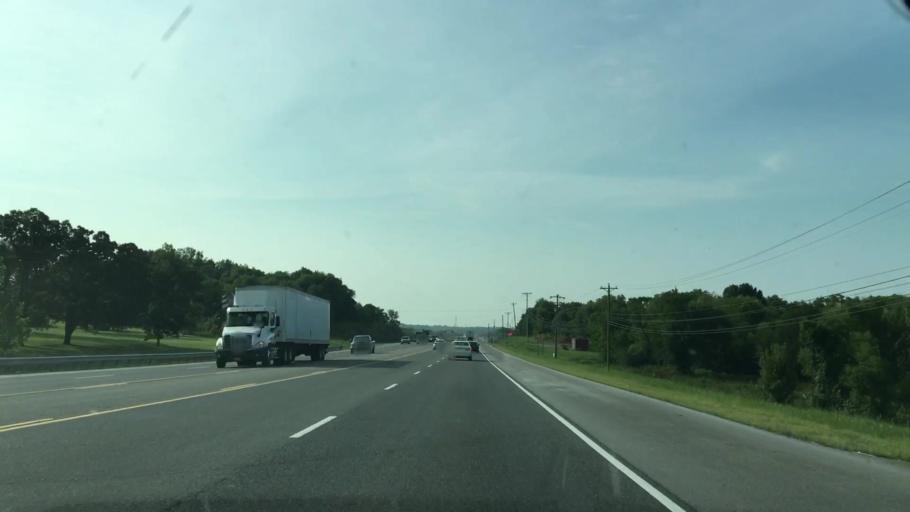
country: US
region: Tennessee
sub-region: Wilson County
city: Rural Hill
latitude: 36.1970
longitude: -86.4137
